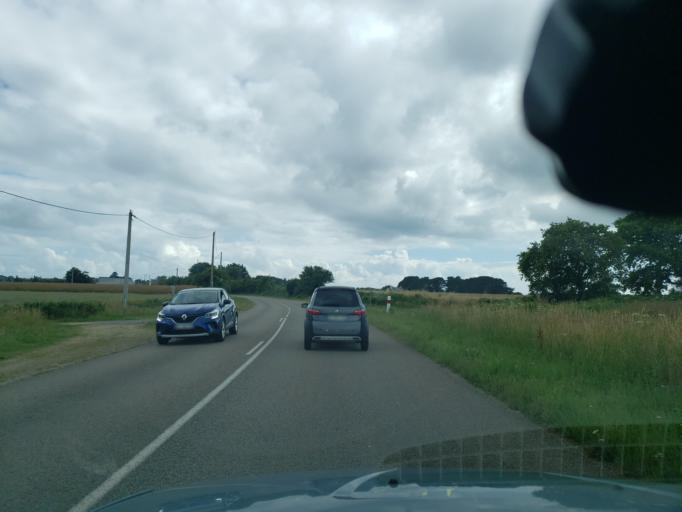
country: FR
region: Brittany
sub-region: Departement du Finistere
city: Plomeur
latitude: 47.8535
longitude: -4.2850
